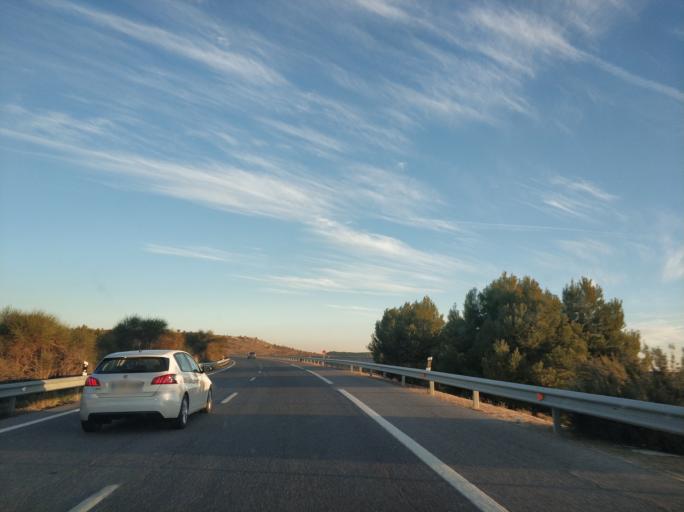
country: ES
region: Madrid
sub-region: Provincia de Madrid
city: Valdemoro
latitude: 40.2181
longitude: -3.6649
